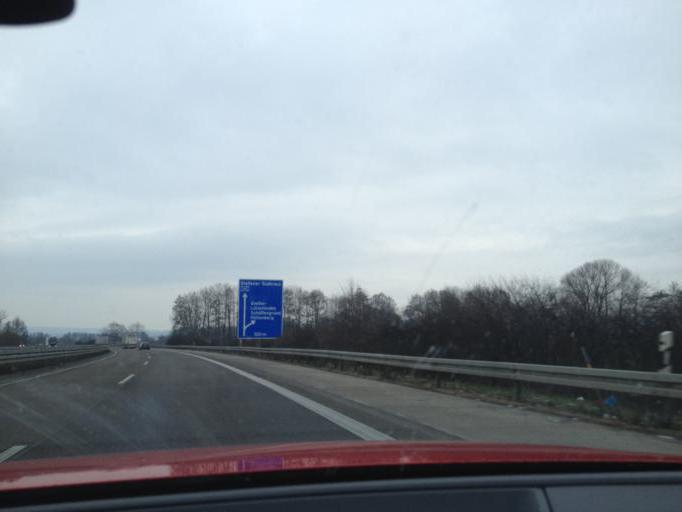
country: DE
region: Hesse
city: Allendorf an der Lahn
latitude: 50.5323
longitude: 8.5859
